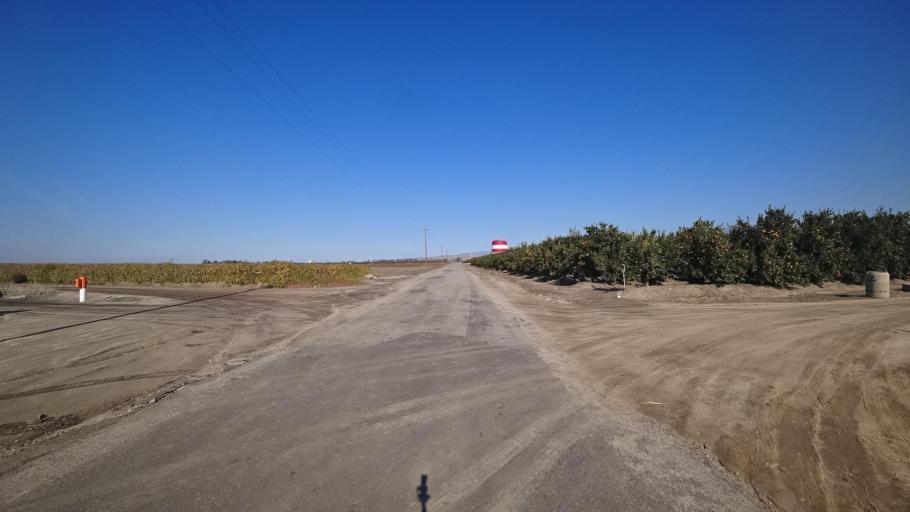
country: US
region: California
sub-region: Kern County
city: Arvin
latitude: 35.2821
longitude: -118.7709
